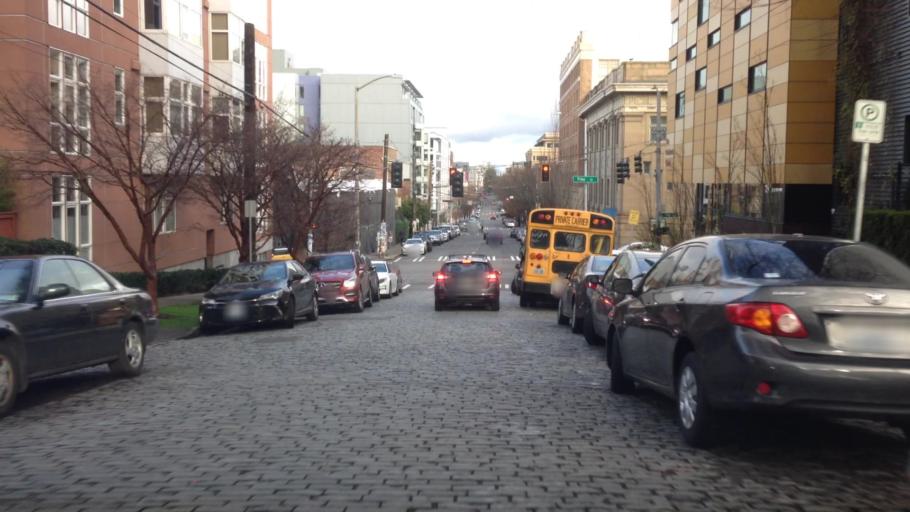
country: US
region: Washington
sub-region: King County
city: Seattle
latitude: 47.6135
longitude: -122.3268
